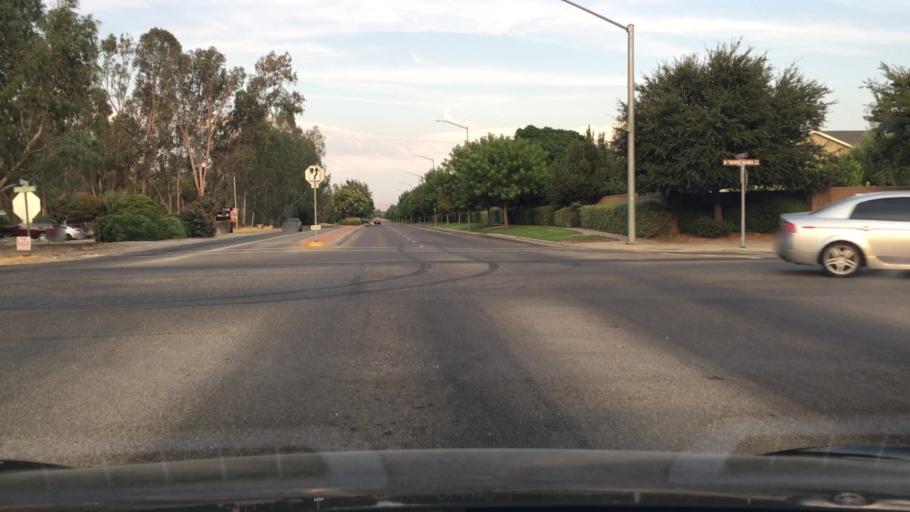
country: US
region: California
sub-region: Fresno County
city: Clovis
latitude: 36.8666
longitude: -119.7113
